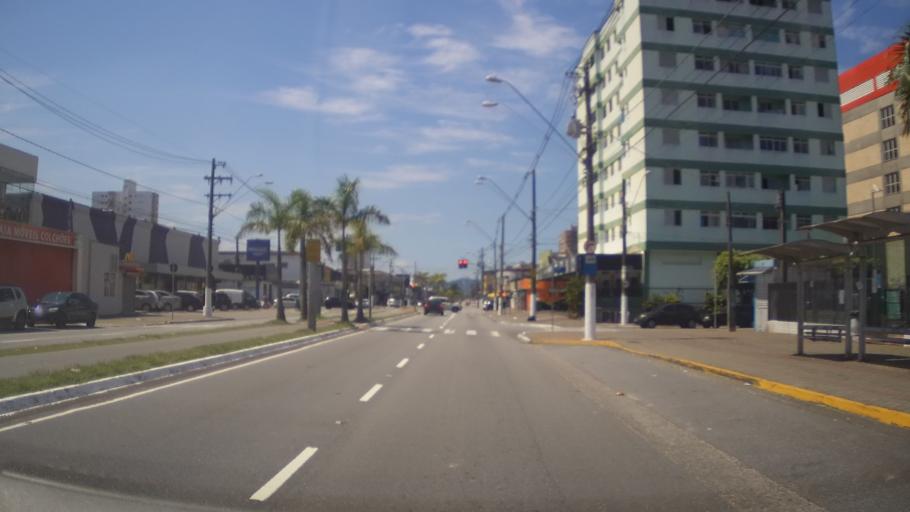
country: BR
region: Sao Paulo
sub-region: Praia Grande
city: Praia Grande
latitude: -24.0193
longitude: -46.4614
